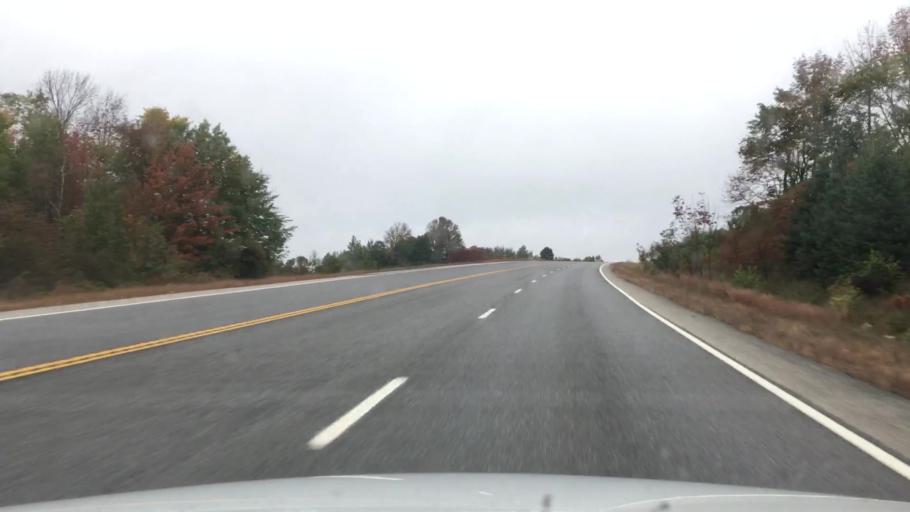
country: US
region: Maine
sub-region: Androscoggin County
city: Poland
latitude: 43.9812
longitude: -70.3678
